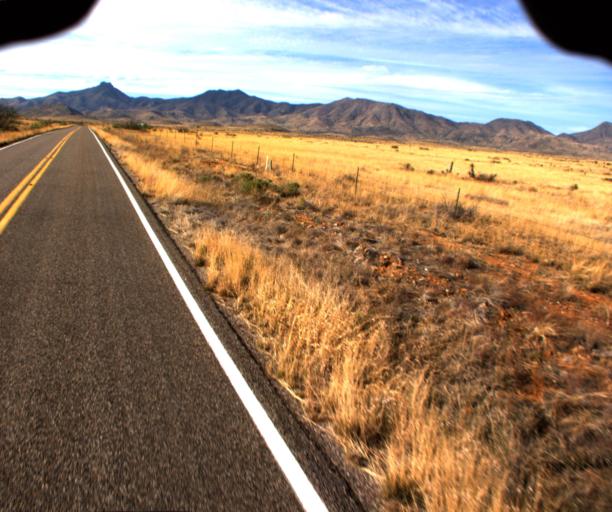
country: US
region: Arizona
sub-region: Cochise County
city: Willcox
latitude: 32.1105
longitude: -109.5490
